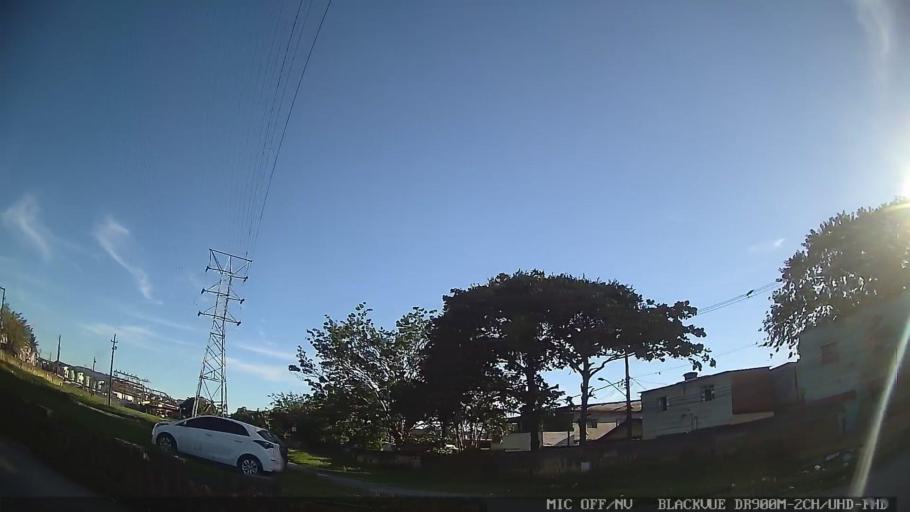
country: BR
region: Sao Paulo
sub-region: Santos
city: Santos
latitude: -23.9497
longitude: -46.3024
